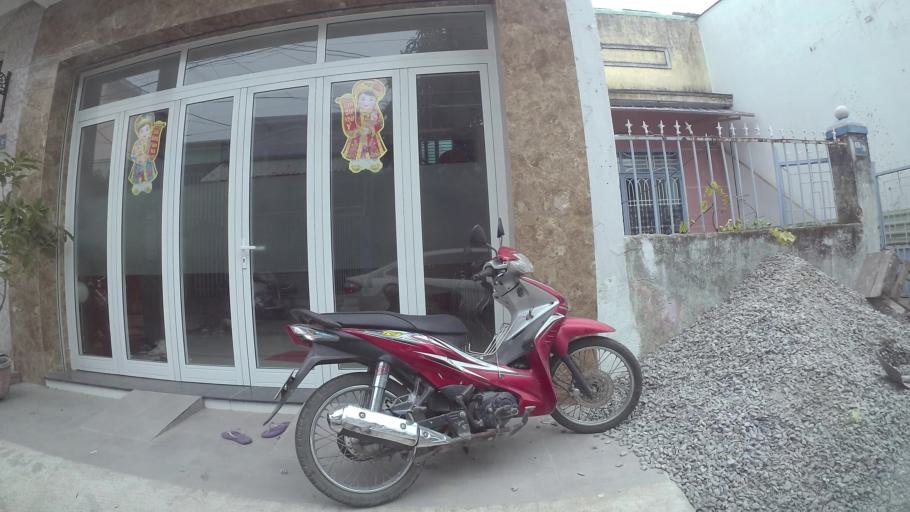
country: VN
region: Da Nang
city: Lien Chieu
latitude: 16.0762
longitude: 108.1740
